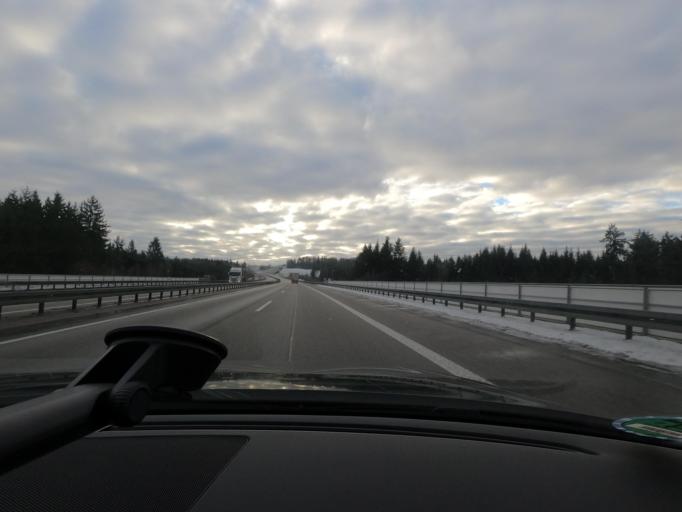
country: DE
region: Thuringia
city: Schleusingen
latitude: 50.4756
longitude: 10.8229
